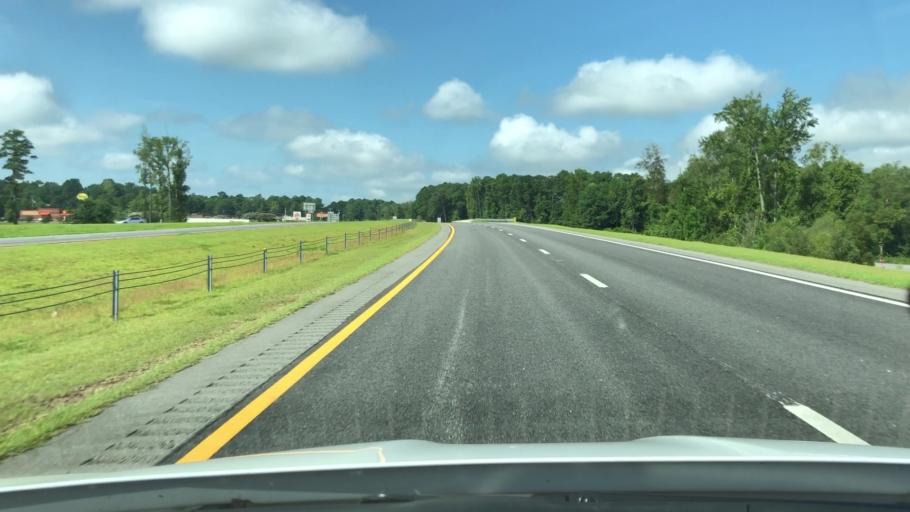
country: US
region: North Carolina
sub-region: Bertie County
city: Windsor
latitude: 36.0120
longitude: -76.9518
